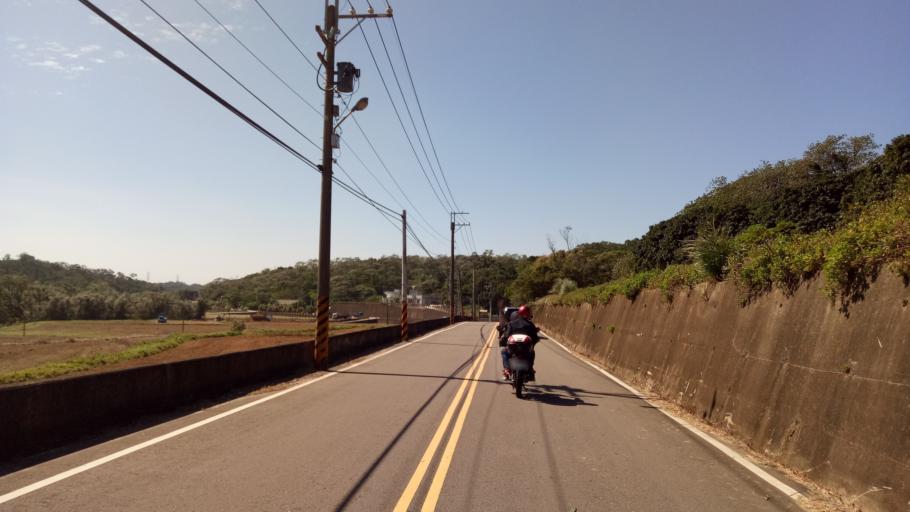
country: TW
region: Taiwan
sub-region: Hsinchu
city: Hsinchu
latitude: 24.7388
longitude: 120.9503
